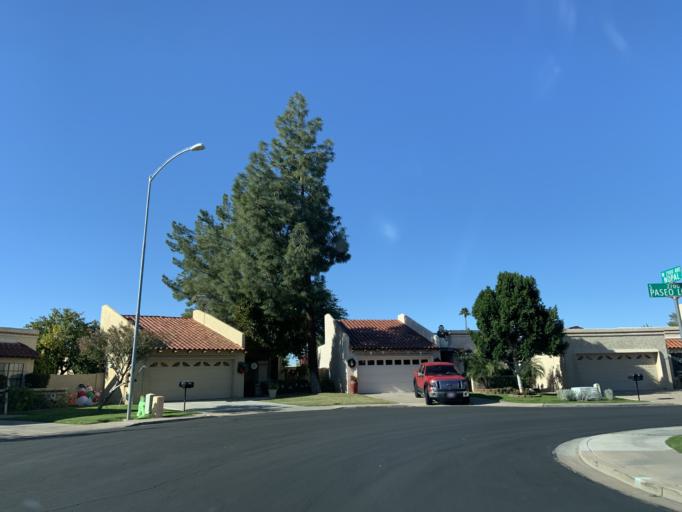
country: US
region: Arizona
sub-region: Maricopa County
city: San Carlos
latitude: 33.3655
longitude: -111.8792
